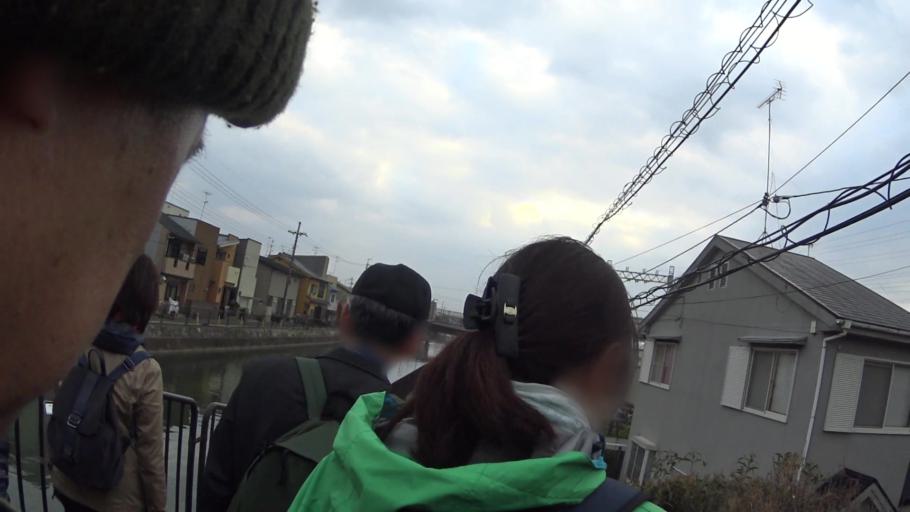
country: JP
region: Kyoto
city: Kyoto
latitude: 34.9611
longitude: 135.7703
